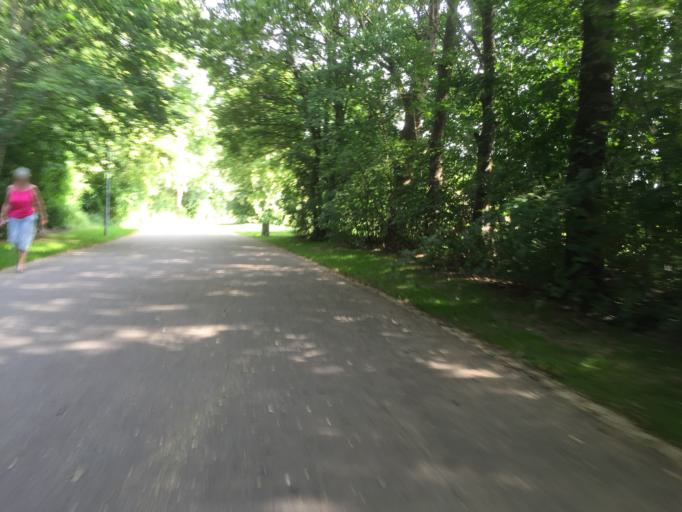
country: DE
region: Bavaria
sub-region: Upper Bavaria
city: Neubiberg
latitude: 48.1104
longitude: 11.6342
